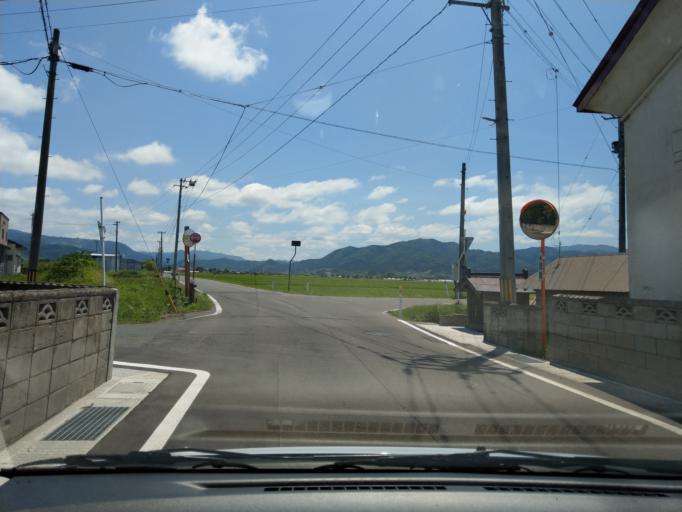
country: JP
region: Aomori
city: Kuroishi
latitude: 40.5733
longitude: 140.5511
